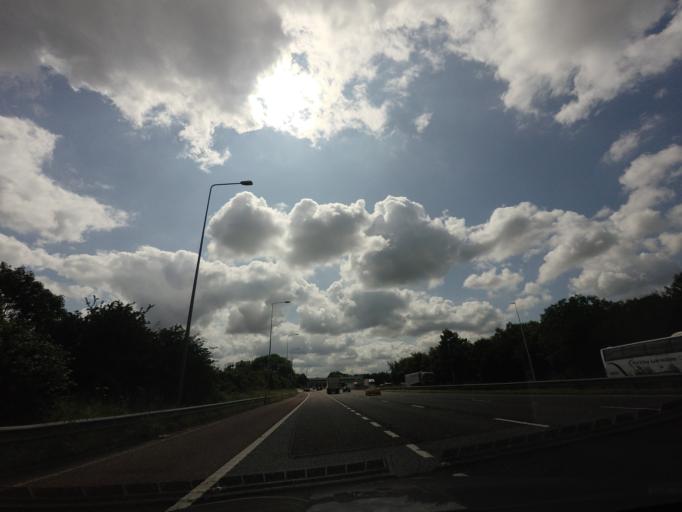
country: GB
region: England
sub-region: Lancashire
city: Coppull
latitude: 53.6343
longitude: -2.6914
